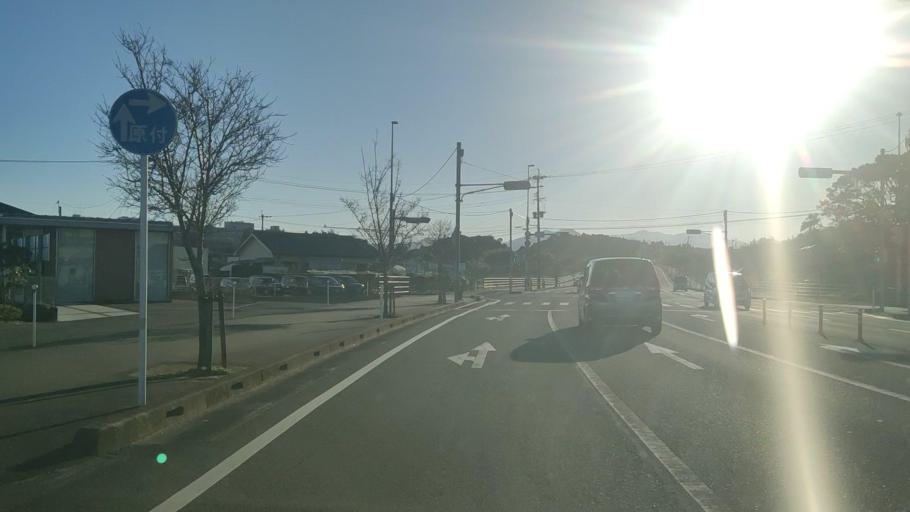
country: JP
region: Miyazaki
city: Miyazaki-shi
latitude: 31.8926
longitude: 131.4061
